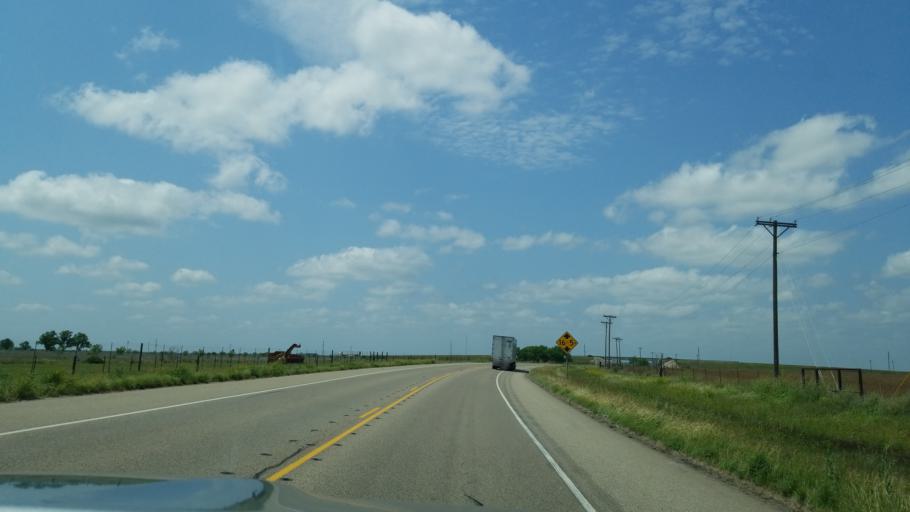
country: US
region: Texas
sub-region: Frio County
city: Pearsall
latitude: 28.9769
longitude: -99.2384
